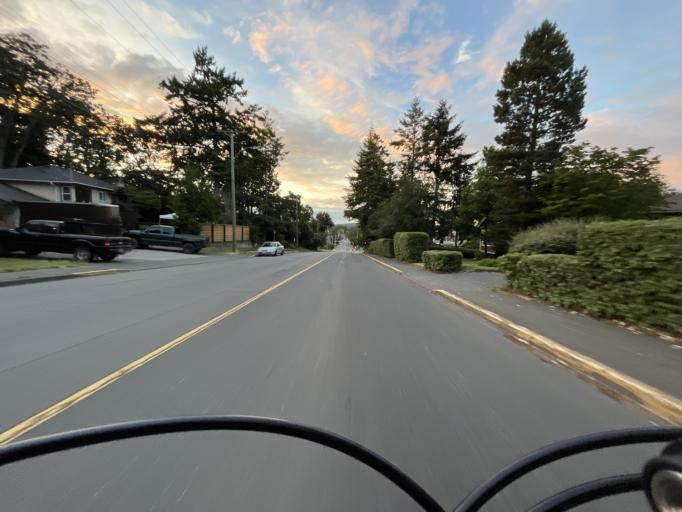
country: CA
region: British Columbia
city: Victoria
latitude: 48.4349
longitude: -123.4032
